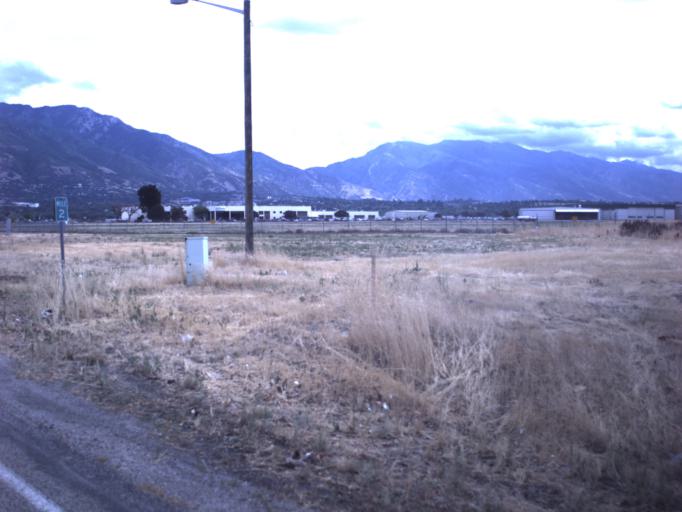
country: US
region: Utah
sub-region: Weber County
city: Riverdale
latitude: 41.2050
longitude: -112.0037
